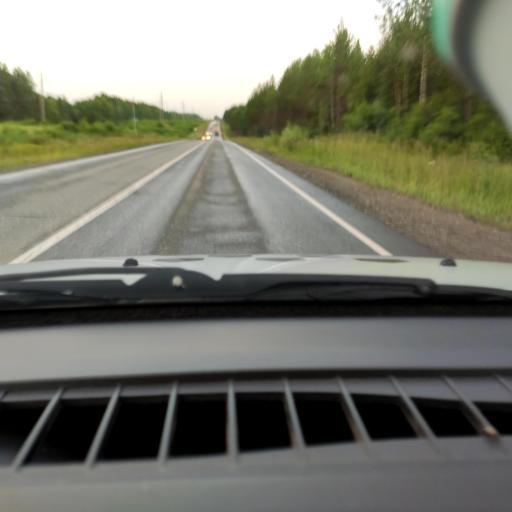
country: RU
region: Udmurtiya
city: Fakel
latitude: 57.6933
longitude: 53.0089
